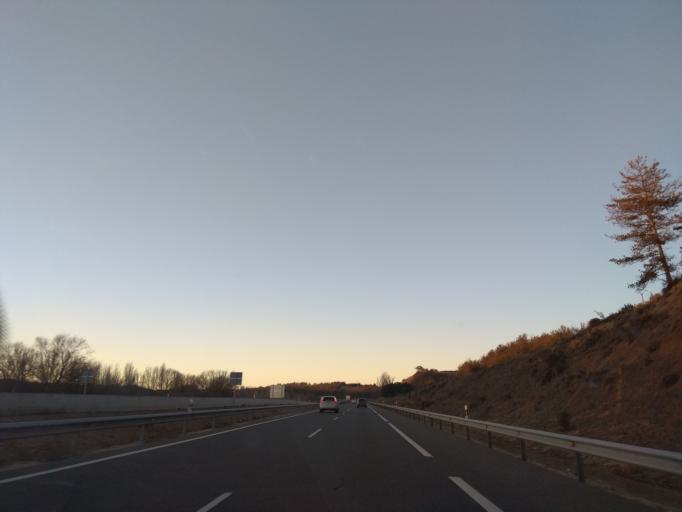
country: ES
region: Castille and Leon
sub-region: Provincia de Burgos
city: Oquillas
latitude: 41.7892
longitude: -3.6985
